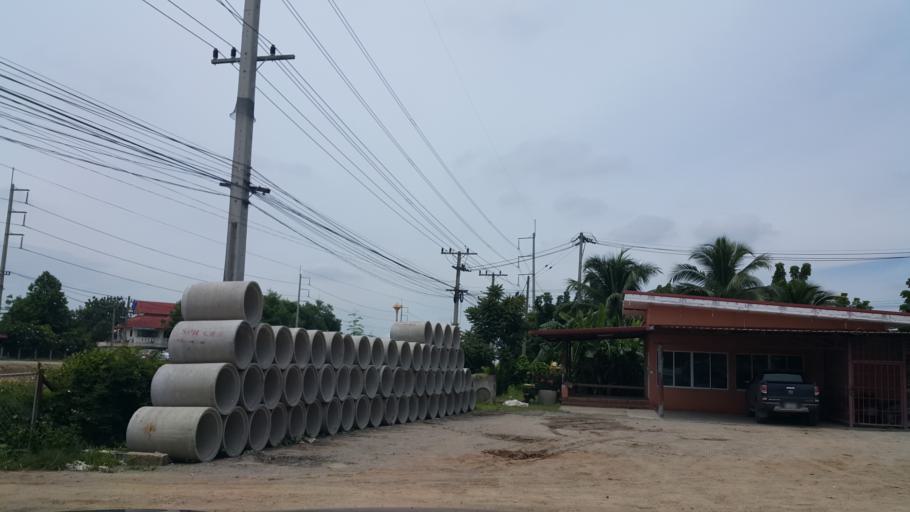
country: TH
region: Chiang Mai
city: Saraphi
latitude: 18.7220
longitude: 99.0078
